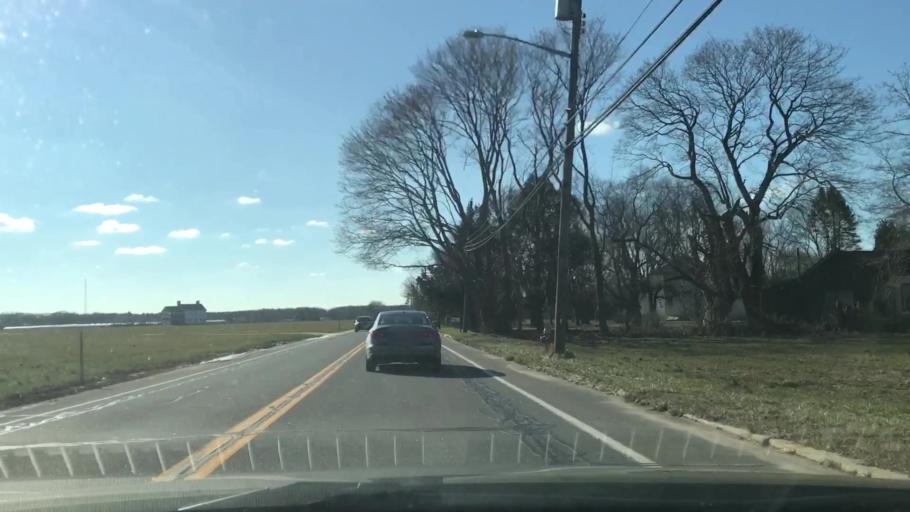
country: US
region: New York
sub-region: Suffolk County
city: Aquebogue
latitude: 40.9512
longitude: -72.6544
